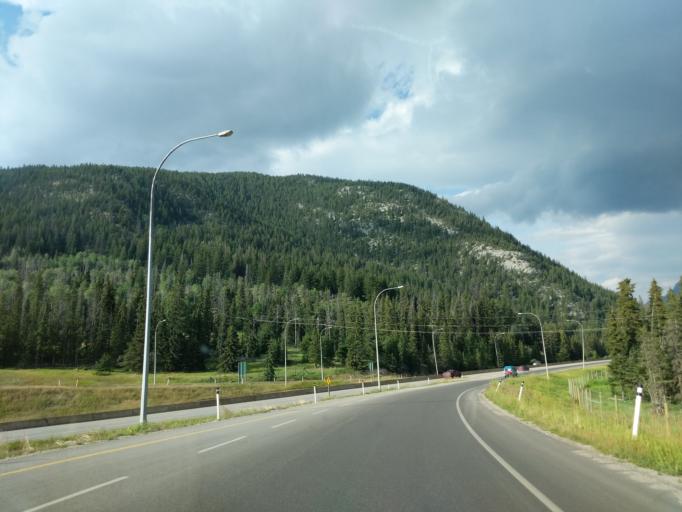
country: CA
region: Alberta
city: Banff
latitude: 51.1878
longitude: -115.5822
